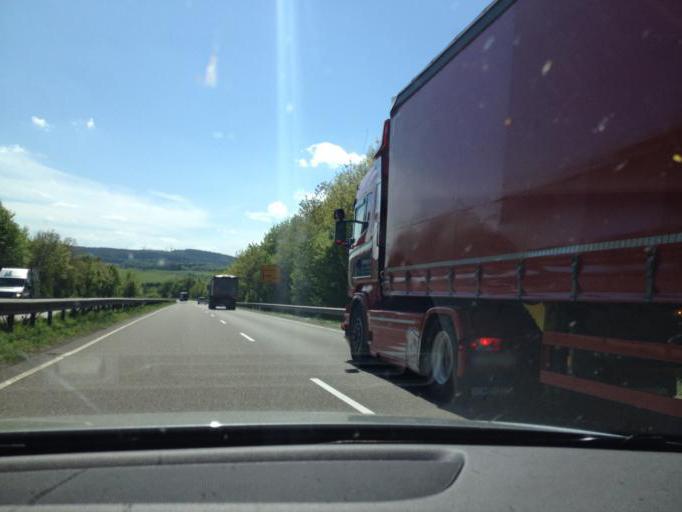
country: DE
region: Rheinland-Pfalz
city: Kerschenbach
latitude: 50.3781
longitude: 6.5139
